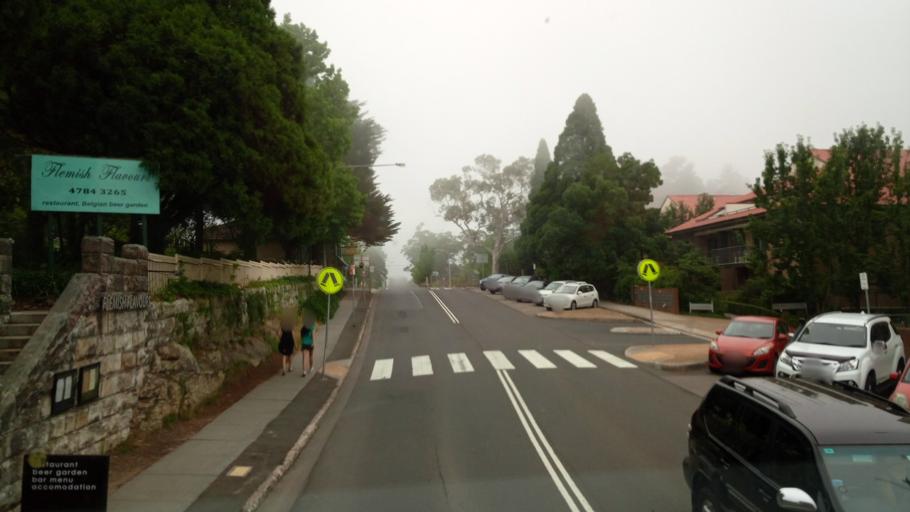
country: AU
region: New South Wales
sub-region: Blue Mountains Municipality
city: Leura
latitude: -33.7120
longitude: 150.3312
